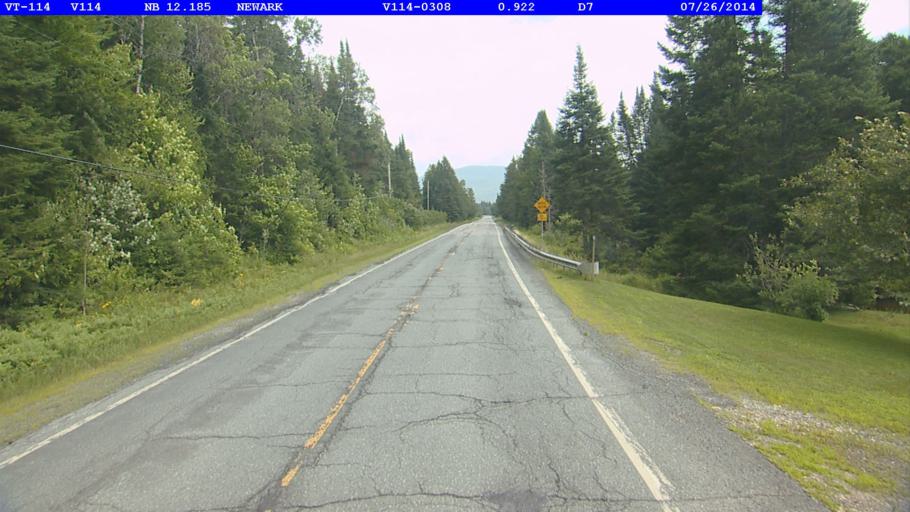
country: US
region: Vermont
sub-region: Caledonia County
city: Lyndonville
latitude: 44.6823
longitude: -71.8800
